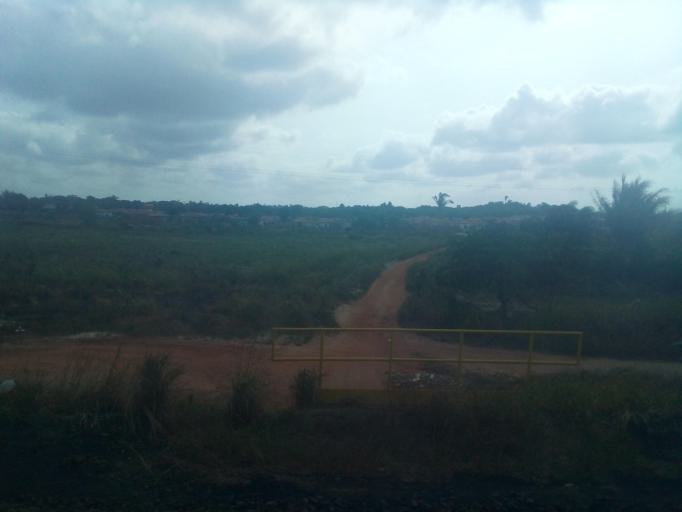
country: BR
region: Maranhao
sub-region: Sao Luis
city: Sao Luis
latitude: -2.6400
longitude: -44.3058
